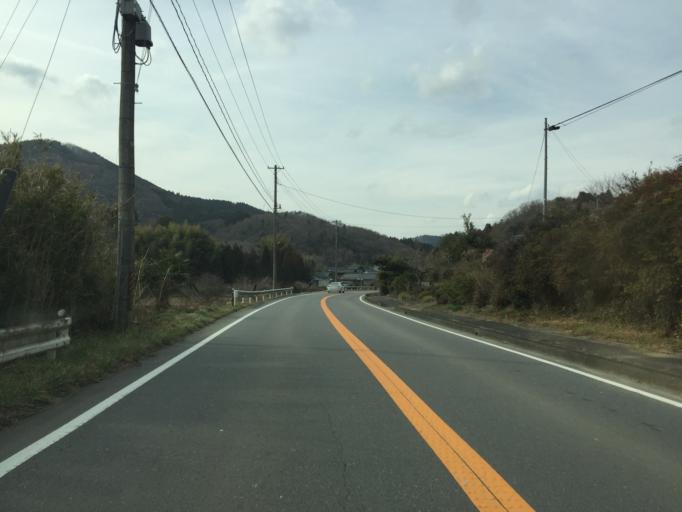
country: JP
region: Fukushima
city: Iwaki
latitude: 36.9647
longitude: 140.7499
